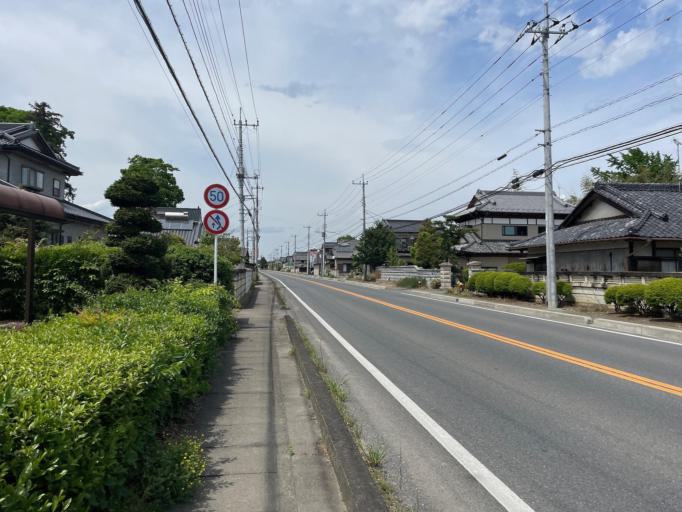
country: JP
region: Tochigi
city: Mibu
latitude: 36.4523
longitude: 139.7755
